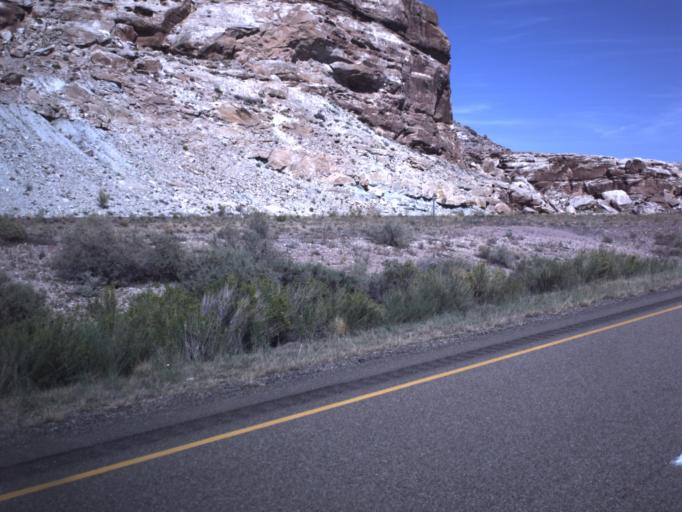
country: US
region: Utah
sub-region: Carbon County
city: East Carbon City
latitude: 38.9213
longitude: -110.3945
